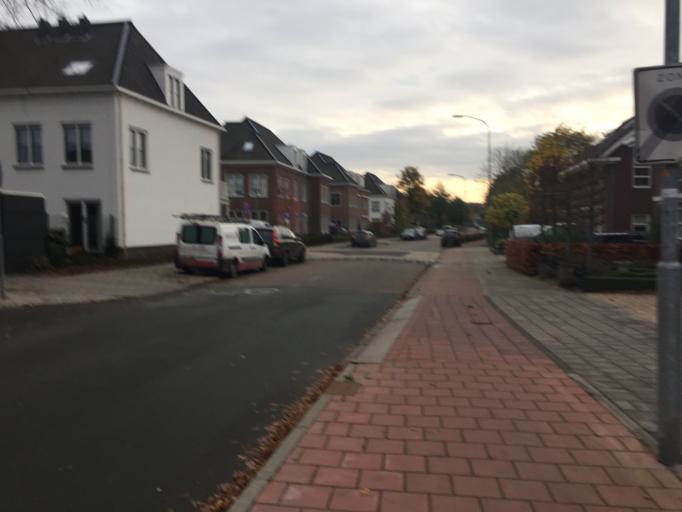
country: NL
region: Utrecht
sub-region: Gemeente Utrechtse Heuvelrug
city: Overberg
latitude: 52.0781
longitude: 5.4967
